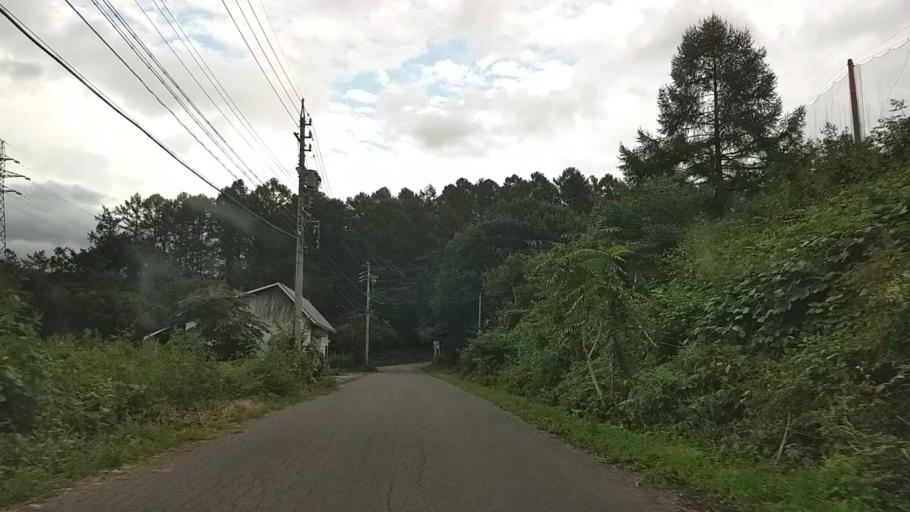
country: JP
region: Nagano
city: Iiyama
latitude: 36.8206
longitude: 138.3953
